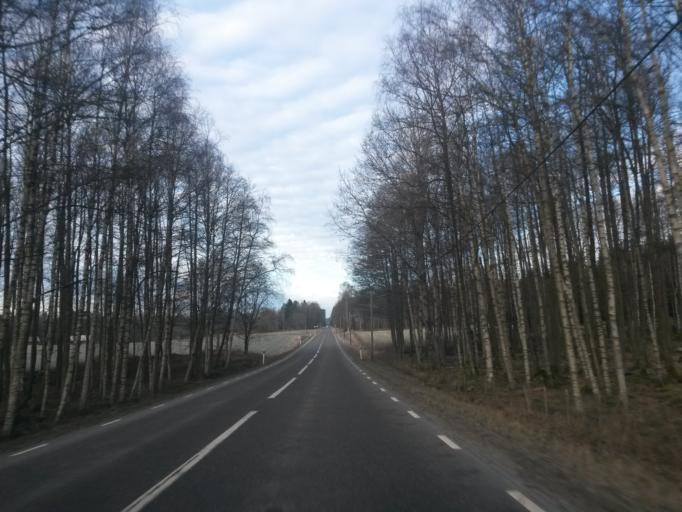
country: SE
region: Vaestra Goetaland
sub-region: Vargarda Kommun
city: Vargarda
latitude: 57.9285
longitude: 12.8582
